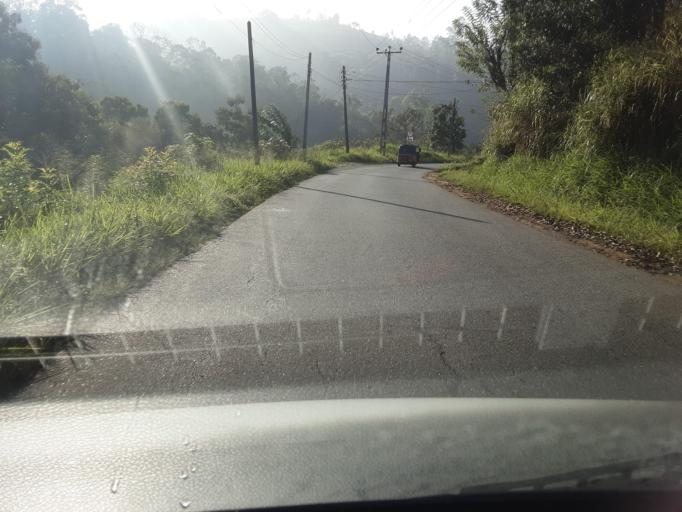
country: LK
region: Uva
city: Haputale
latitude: 6.9093
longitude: 80.9228
